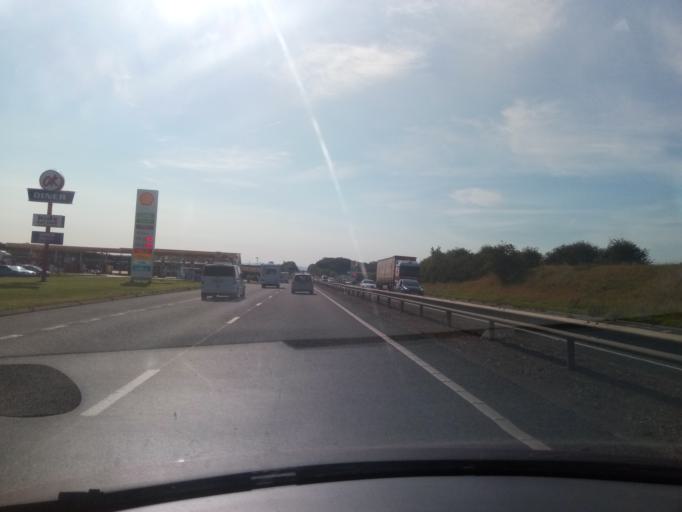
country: GB
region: England
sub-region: Hartlepool
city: Elwick
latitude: 54.6564
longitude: -1.3041
